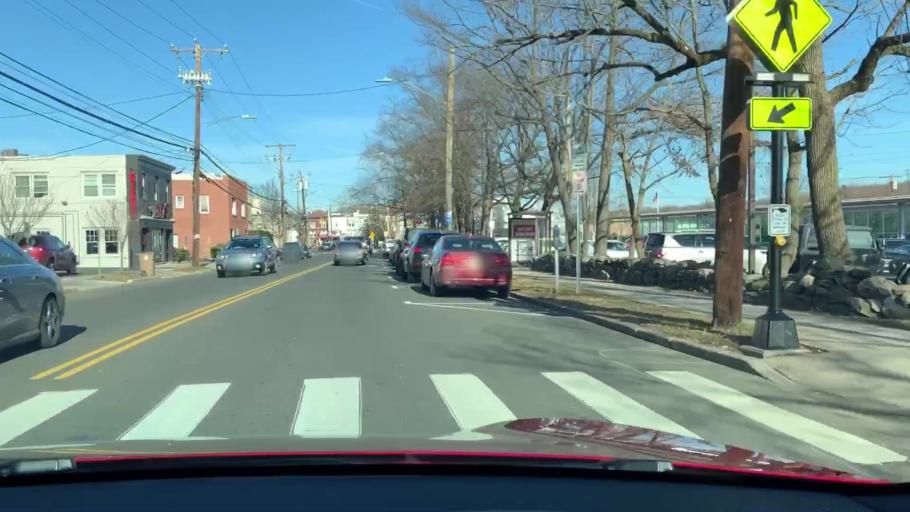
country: US
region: Connecticut
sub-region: Fairfield County
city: Stamford
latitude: 41.0888
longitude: -73.5184
